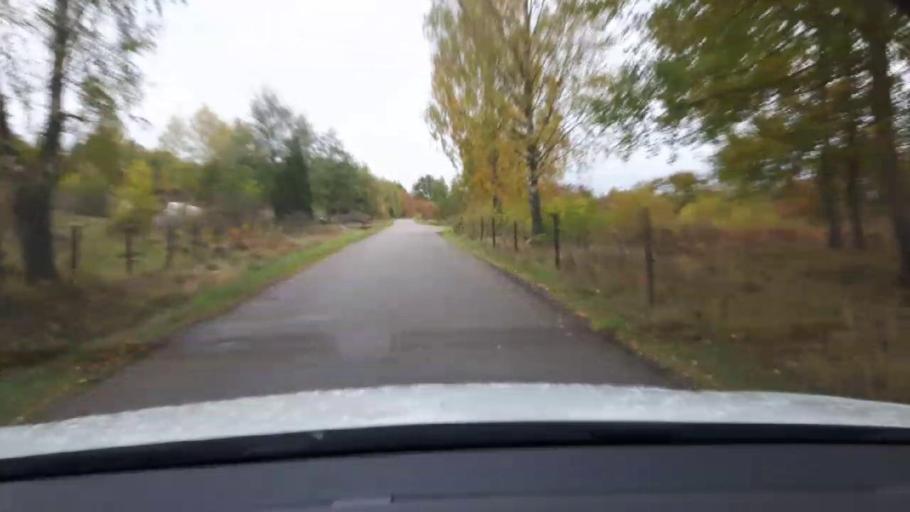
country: SE
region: Kalmar
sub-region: Vimmerby Kommun
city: Sodra Vi
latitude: 57.9572
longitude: 15.9005
